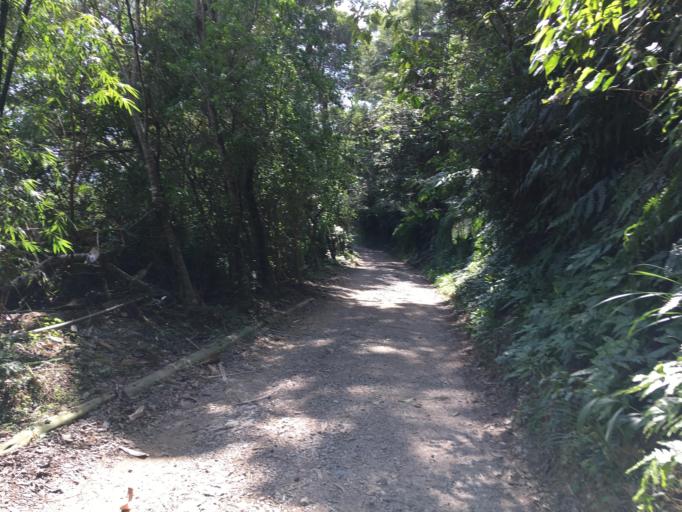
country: TW
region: Taiwan
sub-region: Yilan
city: Yilan
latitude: 24.8407
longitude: 121.7761
